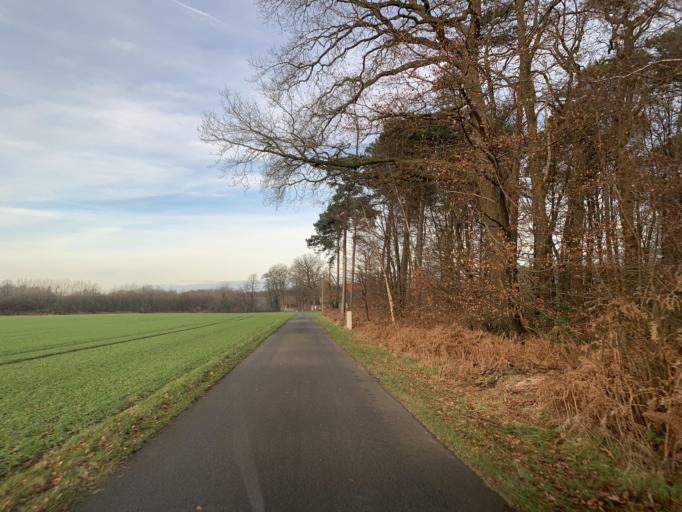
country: DE
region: North Rhine-Westphalia
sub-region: Regierungsbezirk Munster
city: Dulmen
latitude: 51.8041
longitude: 7.3429
